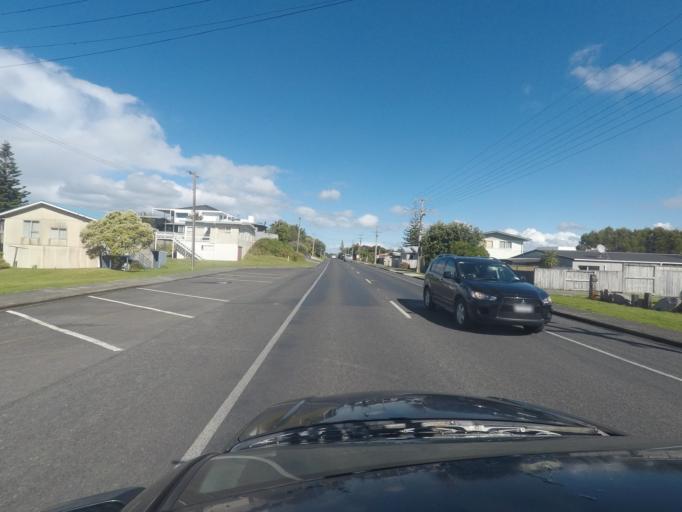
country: NZ
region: Bay of Plenty
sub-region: Western Bay of Plenty District
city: Waihi Beach
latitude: -37.4141
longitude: 175.9469
